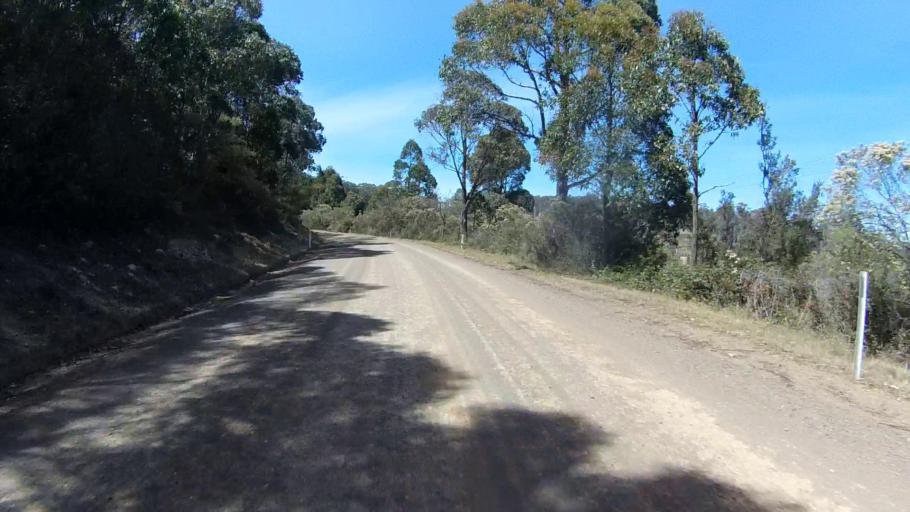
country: AU
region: Tasmania
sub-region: Sorell
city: Sorell
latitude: -42.6986
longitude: 147.7410
